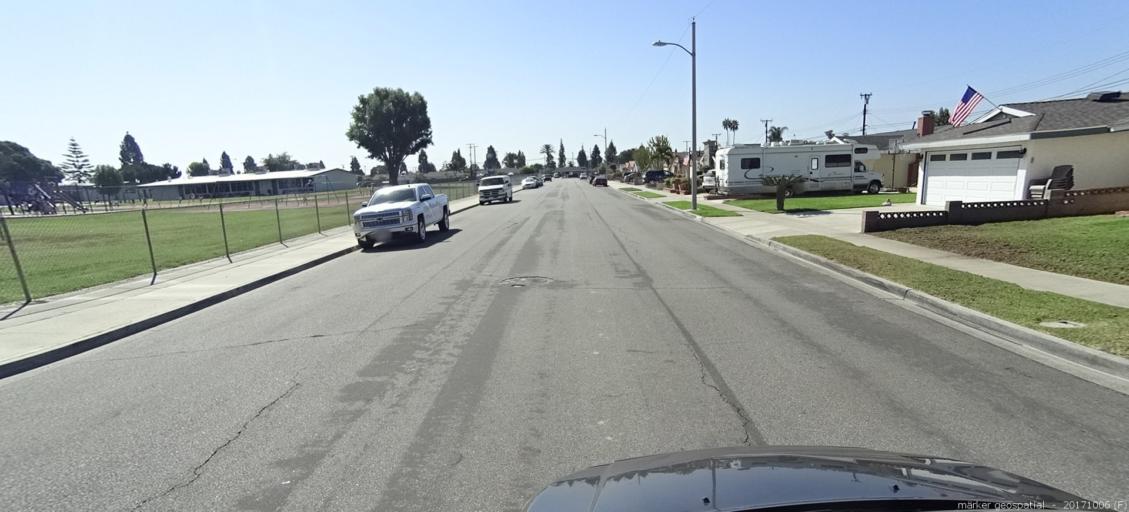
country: US
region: California
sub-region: Orange County
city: Stanton
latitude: 33.7913
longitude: -118.0146
